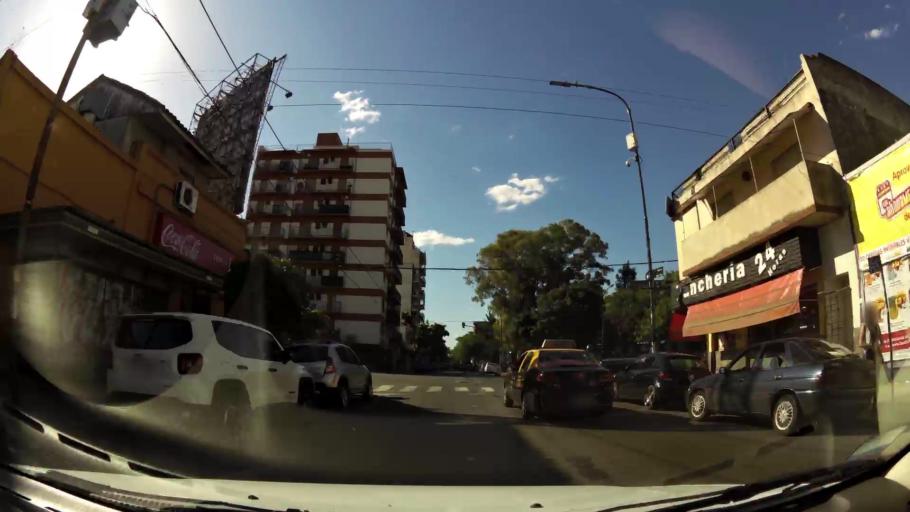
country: AR
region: Buenos Aires F.D.
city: Villa Santa Rita
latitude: -34.6116
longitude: -58.4677
